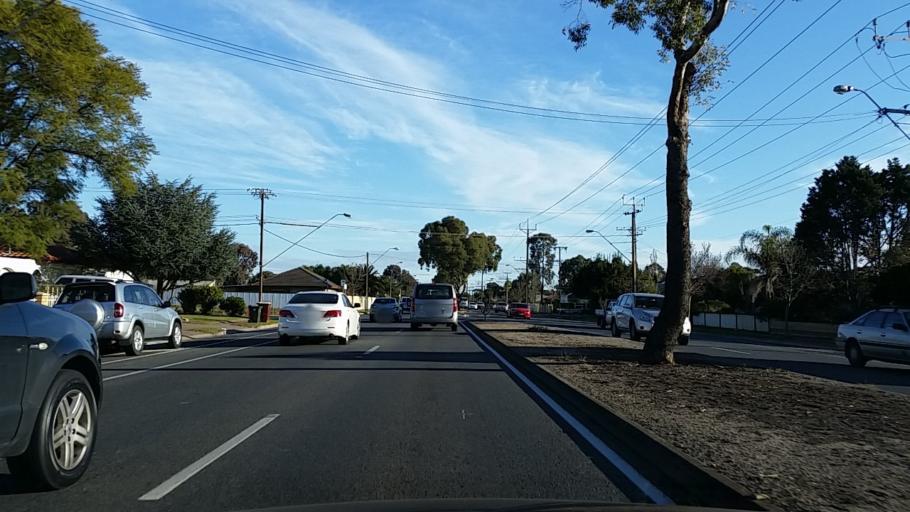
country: AU
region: South Australia
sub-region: Salisbury
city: Salisbury
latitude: -34.7720
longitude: 138.6328
